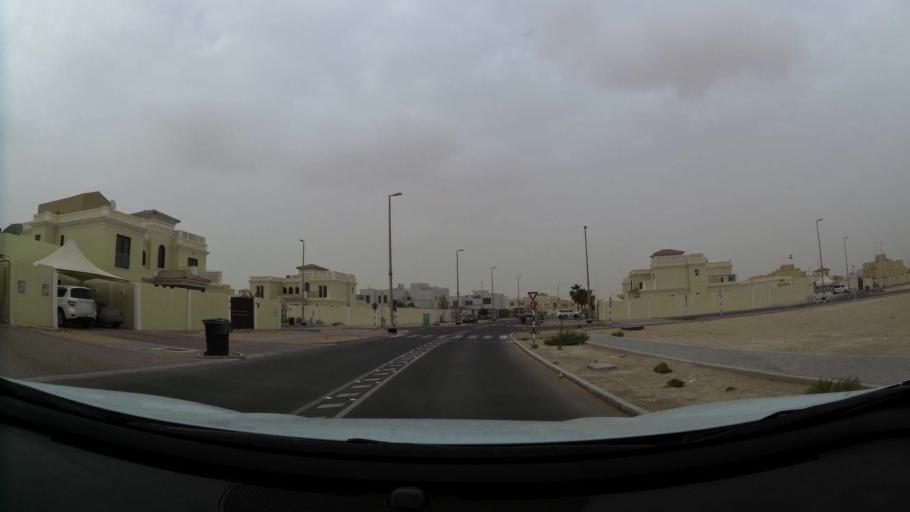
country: AE
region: Abu Dhabi
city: Abu Dhabi
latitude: 24.4340
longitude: 54.7322
